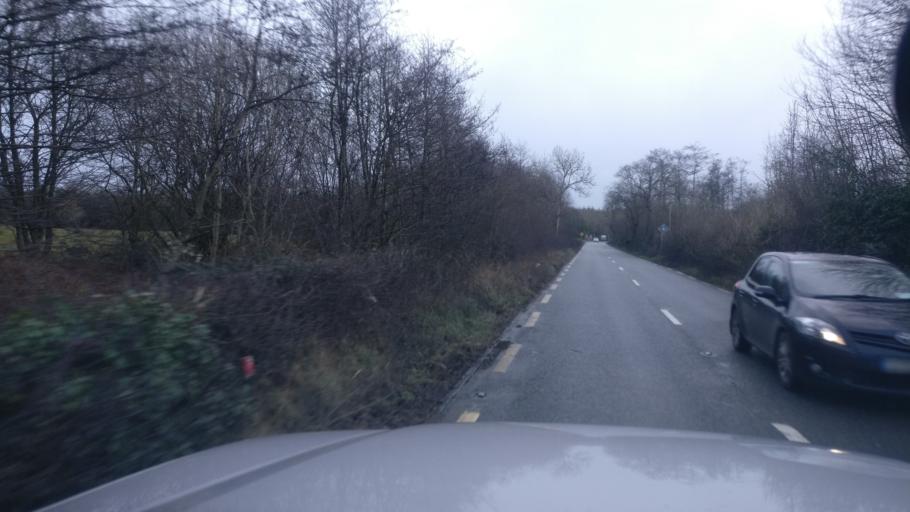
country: IE
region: Connaught
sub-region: County Galway
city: Portumna
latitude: 53.0713
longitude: -8.1488
